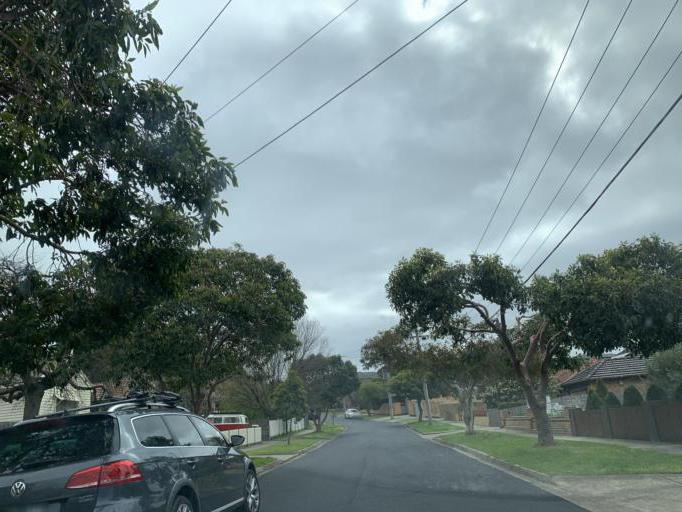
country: AU
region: Victoria
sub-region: Moreland
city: Coburg North
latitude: -37.7291
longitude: 144.9688
